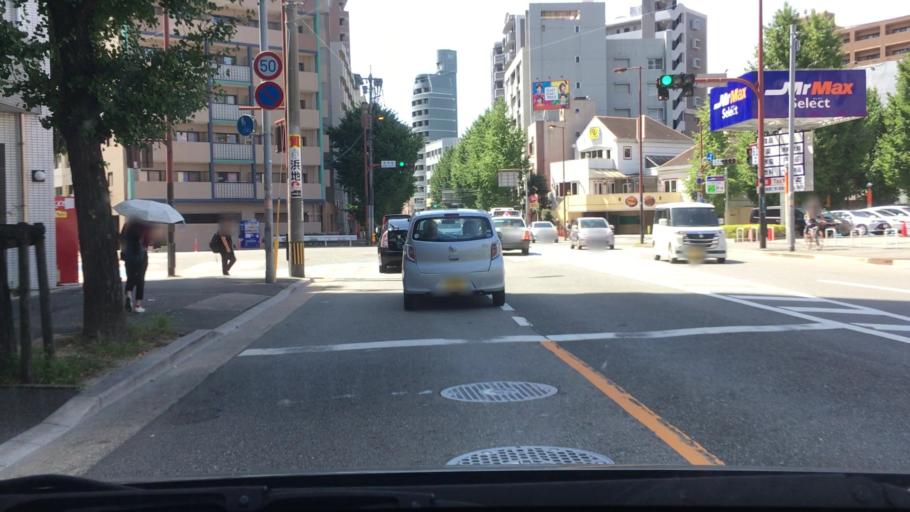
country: JP
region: Fukuoka
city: Fukuoka-shi
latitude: 33.5792
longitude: 130.4199
